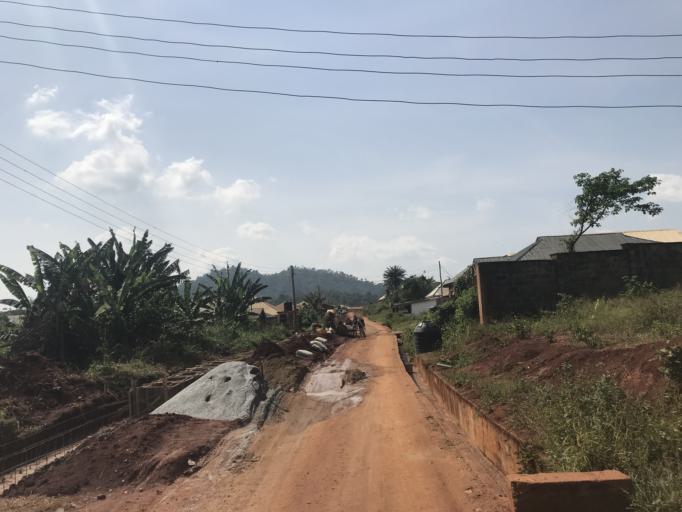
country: NG
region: Osun
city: Ilesa
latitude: 7.6214
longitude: 4.7029
